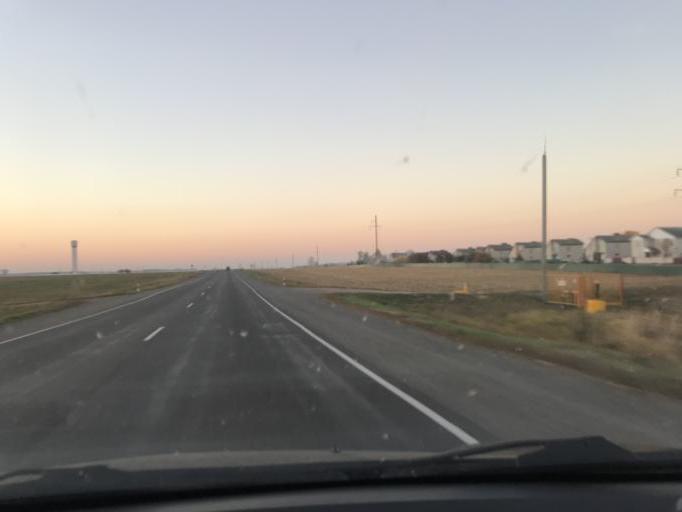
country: BY
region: Gomel
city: Horad Rechytsa
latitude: 52.2545
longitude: 30.4914
